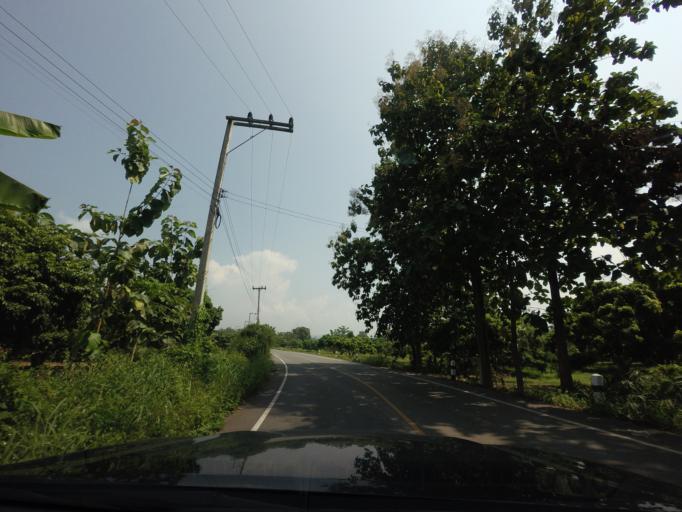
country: TH
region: Nan
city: Nan
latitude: 18.8562
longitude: 100.8050
